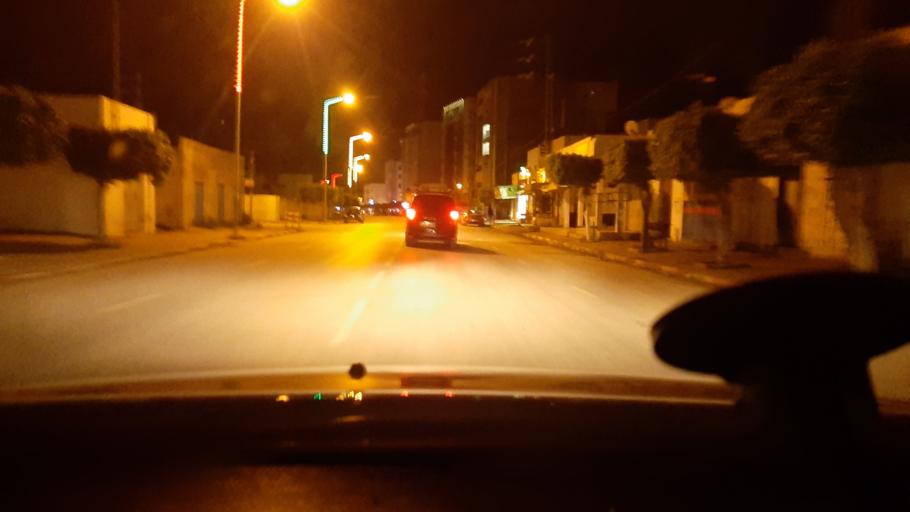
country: TN
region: Safaqis
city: Sfax
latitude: 34.7825
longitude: 10.7227
